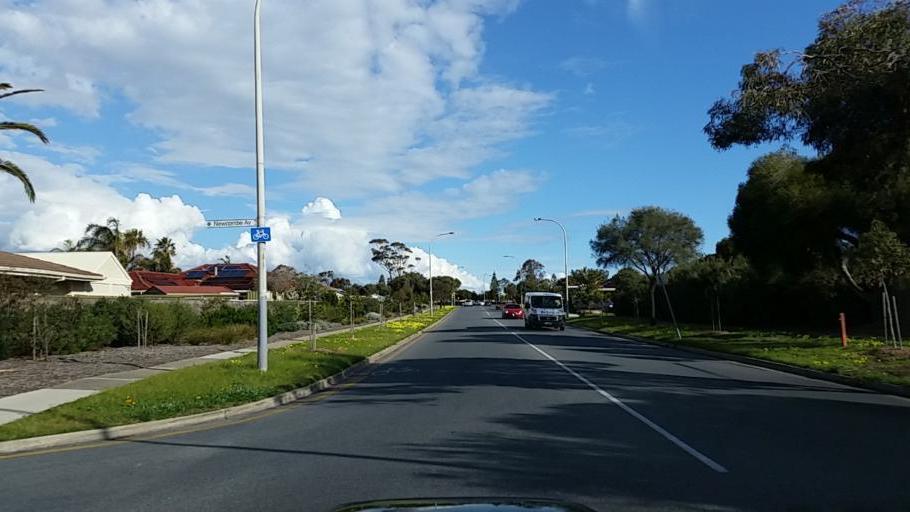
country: AU
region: South Australia
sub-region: Charles Sturt
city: West Lakes Shore
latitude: -34.8692
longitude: 138.4837
